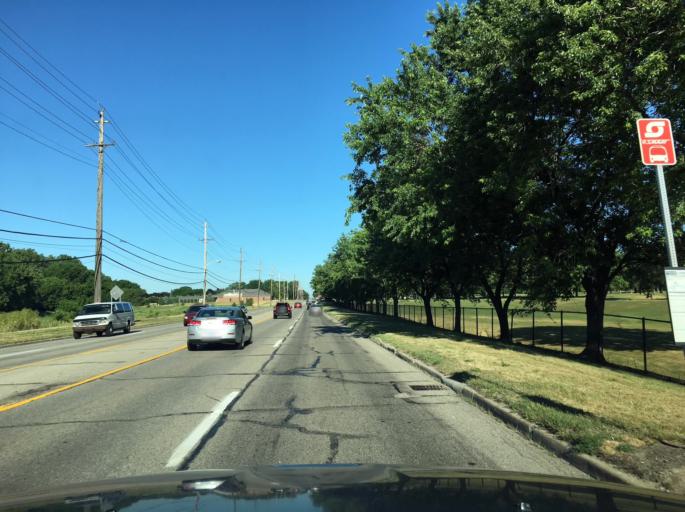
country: US
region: Michigan
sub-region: Macomb County
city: Sterling Heights
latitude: 42.5373
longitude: -83.0080
